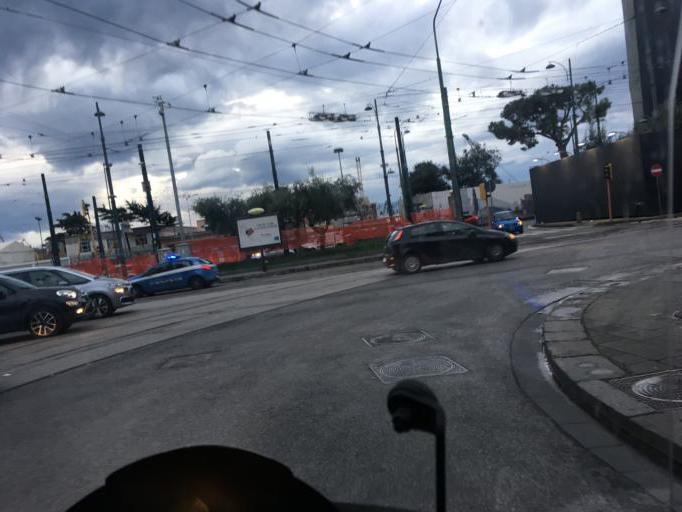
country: IT
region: Campania
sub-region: Provincia di Napoli
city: Napoli
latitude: 40.8466
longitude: 14.2691
